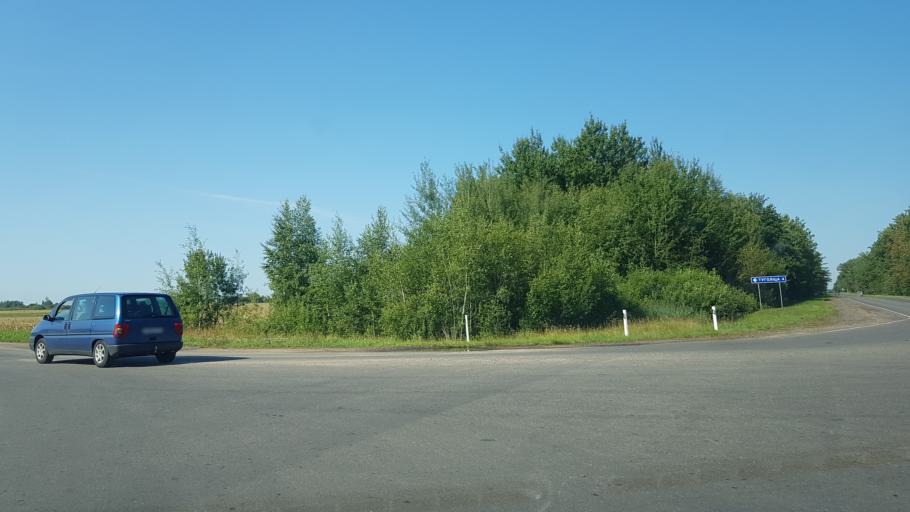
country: BY
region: Mogilev
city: Babruysk
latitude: 53.1066
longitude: 29.1690
